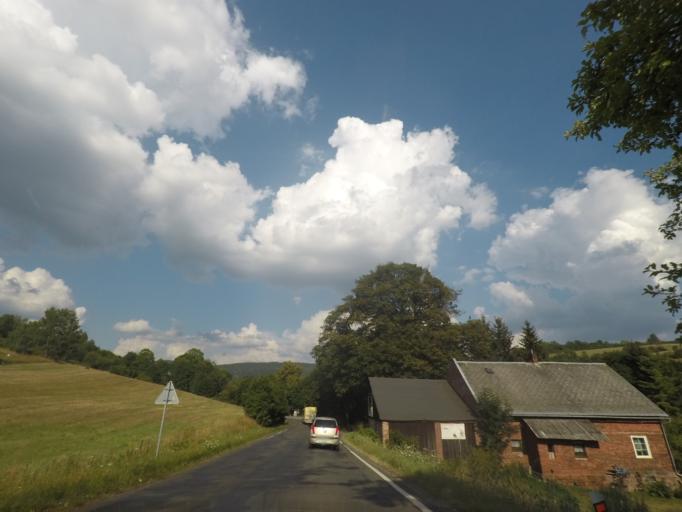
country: CZ
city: Radvanice
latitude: 50.5971
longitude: 16.0241
